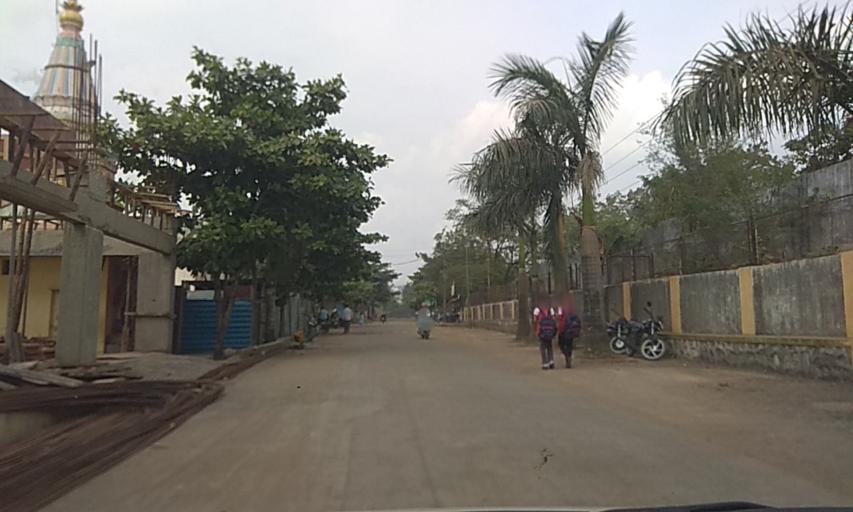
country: IN
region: Maharashtra
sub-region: Pune Division
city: Pimpri
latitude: 18.5760
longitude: 73.7092
